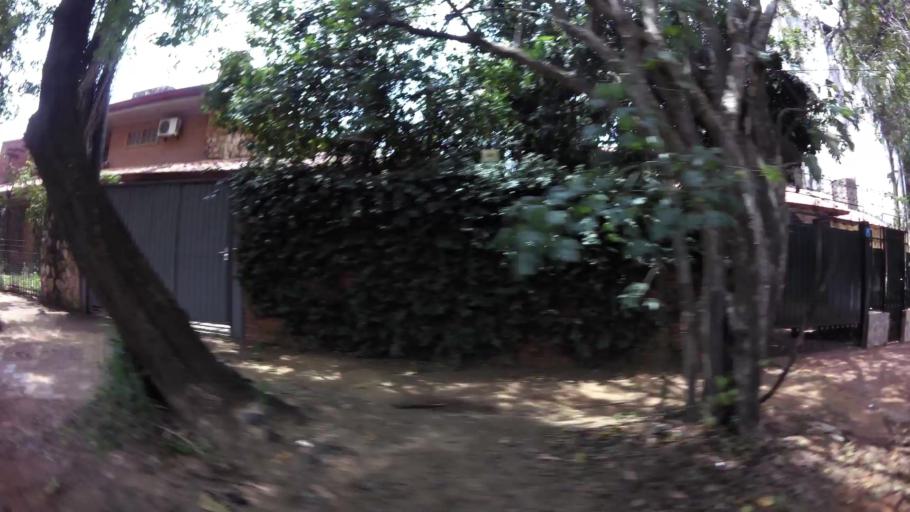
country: PY
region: Central
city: Fernando de la Mora
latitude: -25.3071
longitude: -57.5589
